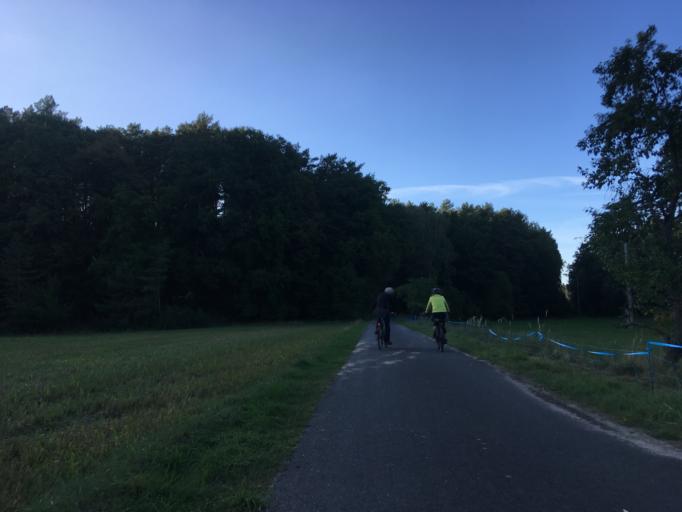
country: PL
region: Lubusz
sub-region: Powiat zarski
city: Trzebiel
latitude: 51.6245
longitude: 14.7553
